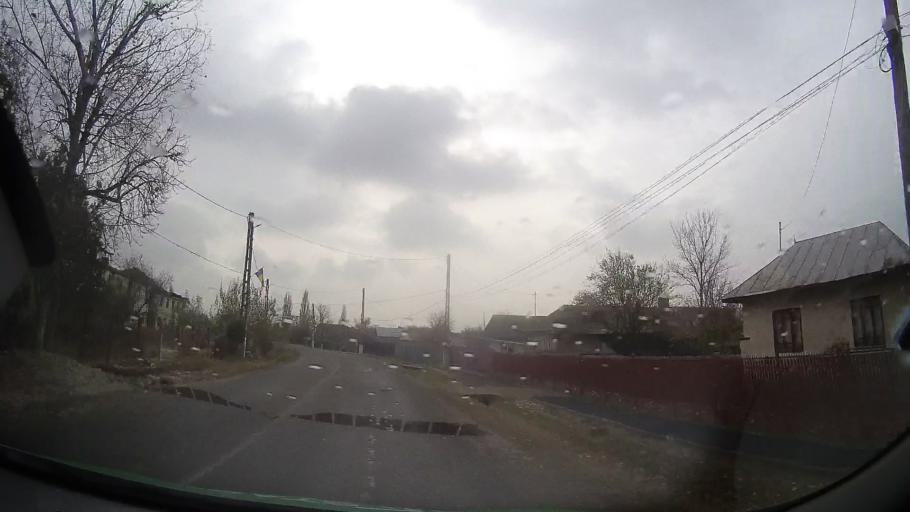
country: RO
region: Prahova
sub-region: Comuna Draganesti
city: Draganesti
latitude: 44.8392
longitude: 26.2690
